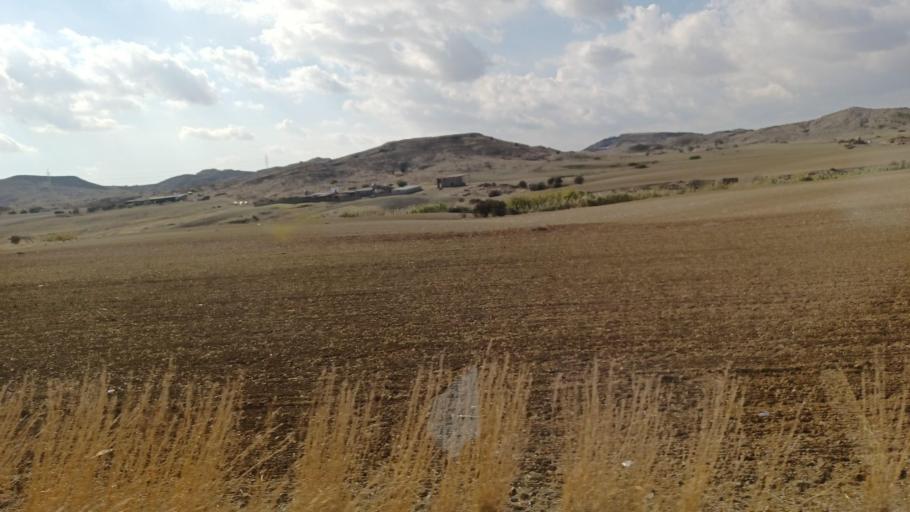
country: CY
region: Larnaka
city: Voroklini
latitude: 35.0109
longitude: 33.6421
